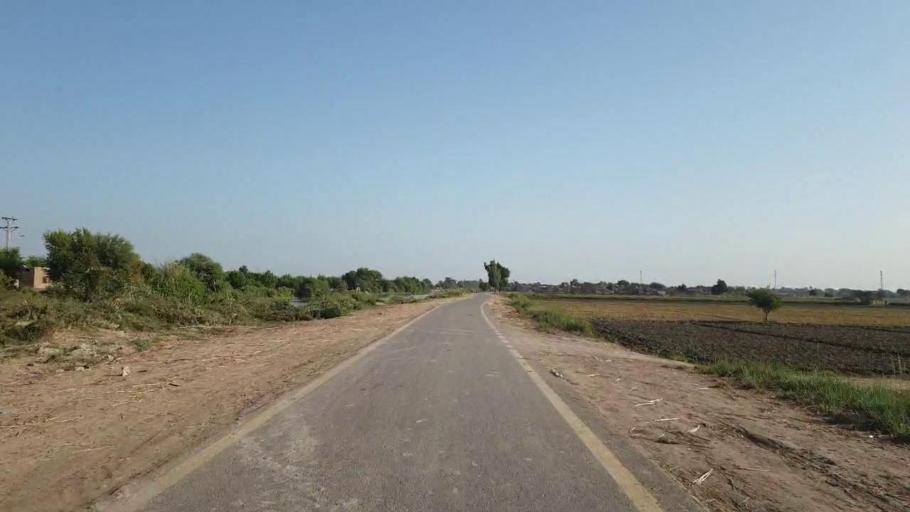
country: PK
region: Sindh
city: Hyderabad
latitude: 25.3279
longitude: 68.4249
